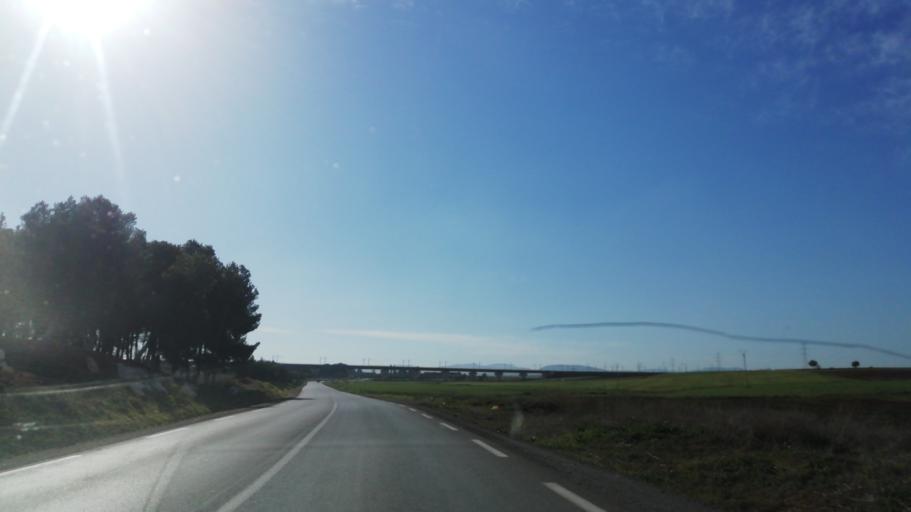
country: DZ
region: Tlemcen
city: Ouled Mimoun
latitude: 35.0129
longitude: -0.9057
